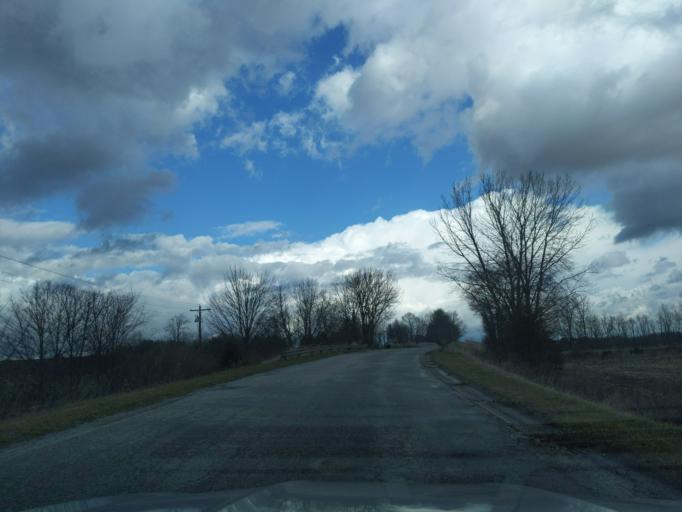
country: US
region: Indiana
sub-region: Decatur County
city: Saint Paul
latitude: 39.4037
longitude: -85.5596
